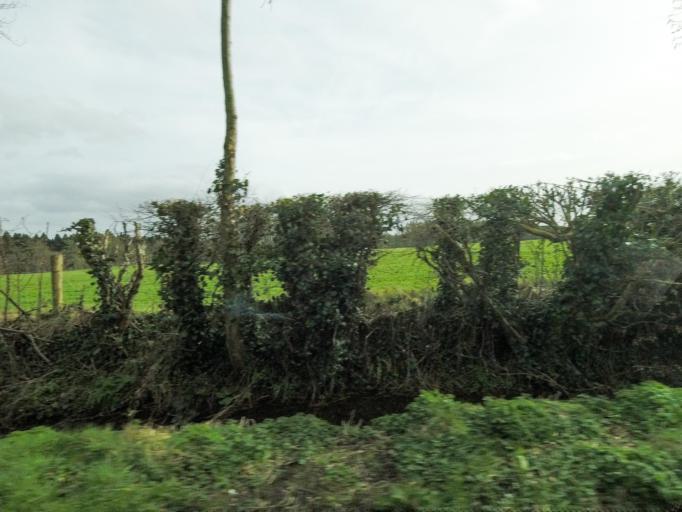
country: IE
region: Leinster
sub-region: Wicklow
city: Blessington
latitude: 53.1600
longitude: -6.5564
